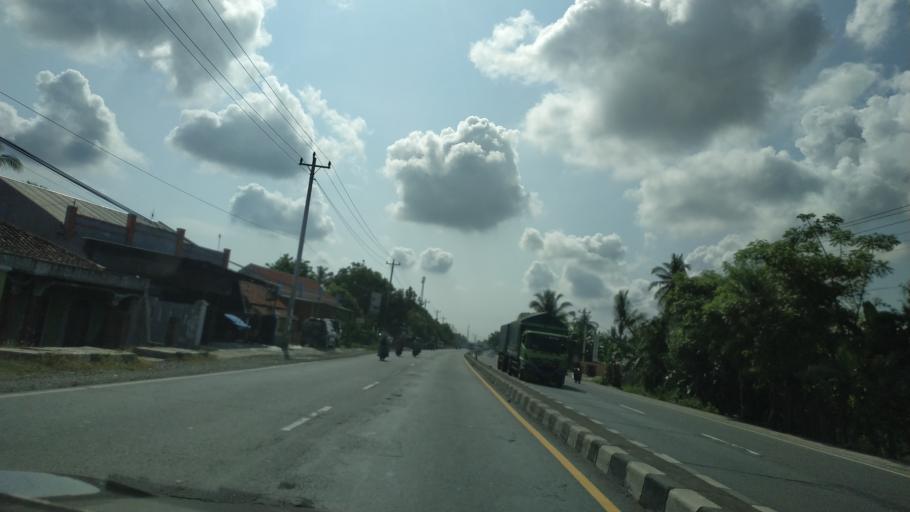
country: ID
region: Central Java
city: Comal
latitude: -6.8869
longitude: 109.5504
